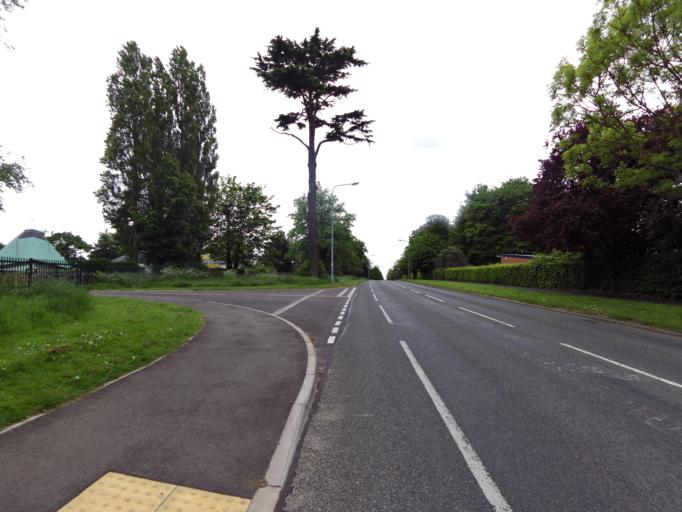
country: GB
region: England
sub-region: Suffolk
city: Ipswich
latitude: 52.0458
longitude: 1.1338
